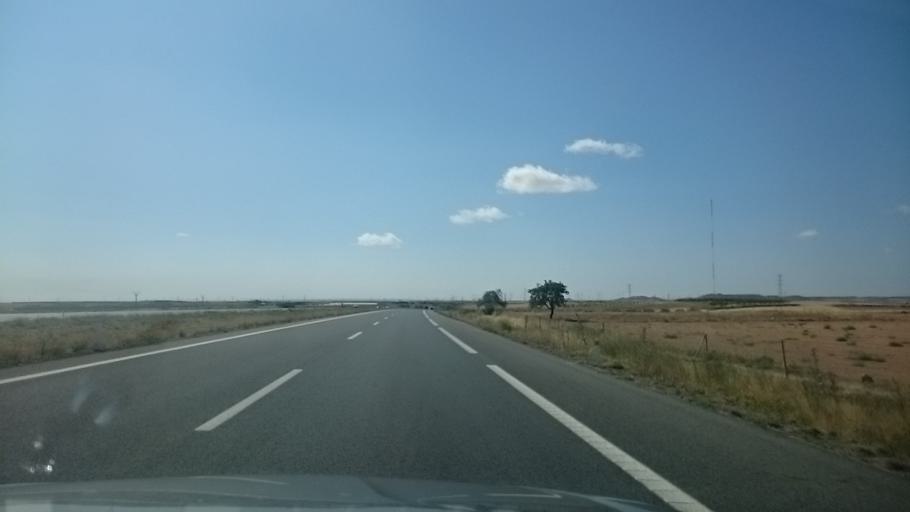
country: ES
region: Aragon
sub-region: Provincia de Zaragoza
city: Mallen
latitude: 41.8715
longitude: -1.3956
